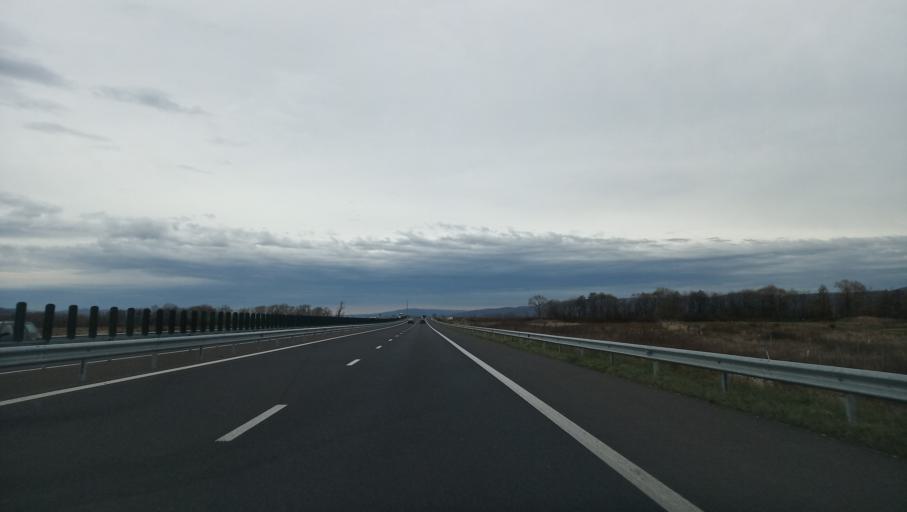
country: RO
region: Hunedoara
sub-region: Comuna Ilia
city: Ilia
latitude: 45.9468
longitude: 22.6976
